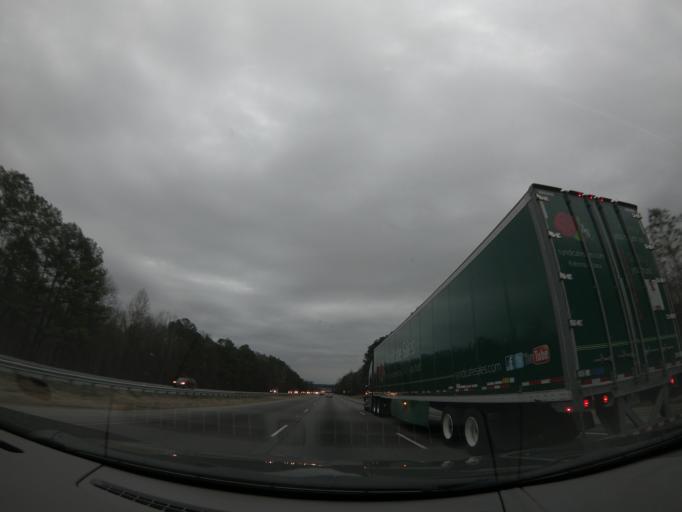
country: US
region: Georgia
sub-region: Gordon County
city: Calhoun
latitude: 34.5938
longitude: -84.9549
